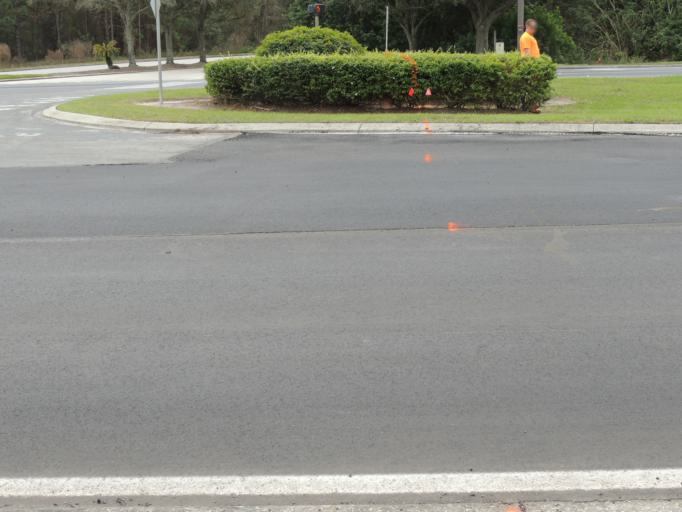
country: US
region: Florida
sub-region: Osceola County
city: Celebration
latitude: 28.3385
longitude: -81.5064
